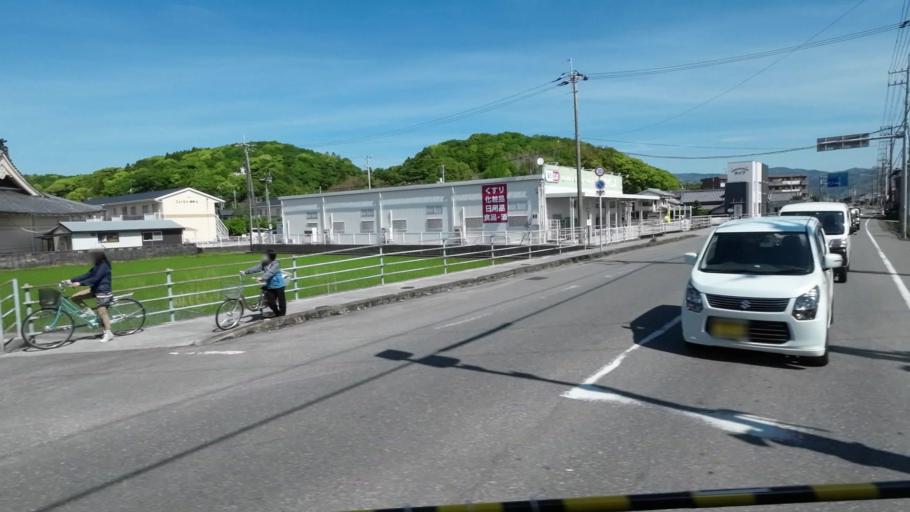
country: JP
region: Kochi
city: Kochi-shi
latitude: 33.5808
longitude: 133.6491
